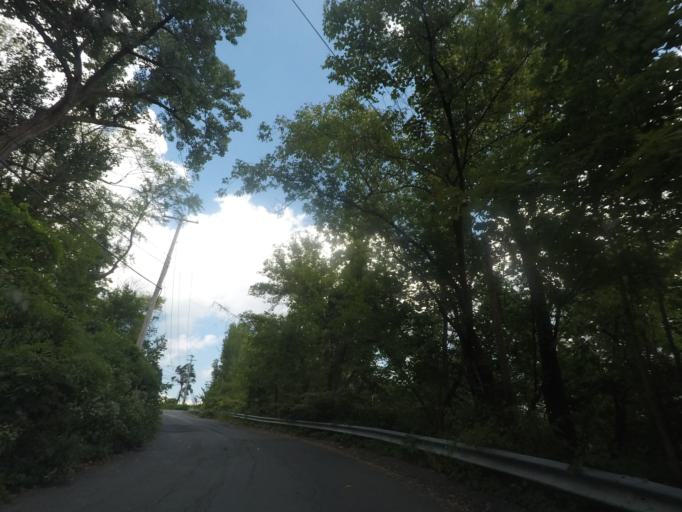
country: US
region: New York
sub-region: Rensselaer County
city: Troy
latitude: 42.7050
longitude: -73.6882
